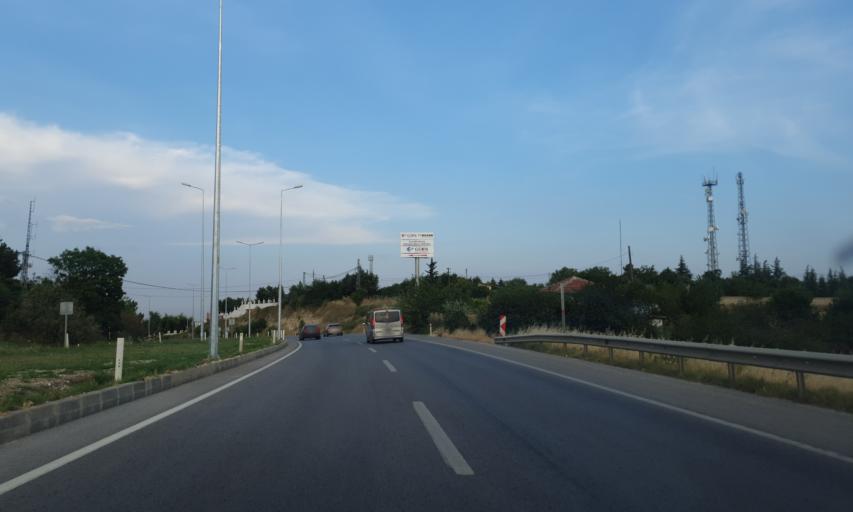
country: TR
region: Kirklareli
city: Luleburgaz
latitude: 41.4041
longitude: 27.3283
